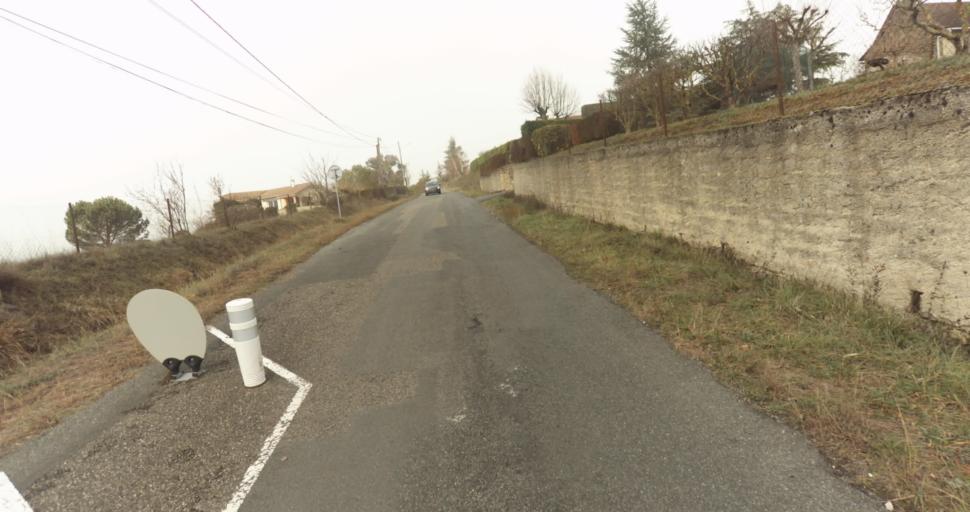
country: FR
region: Midi-Pyrenees
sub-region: Departement du Lot
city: Figeac
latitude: 44.6187
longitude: 2.0248
